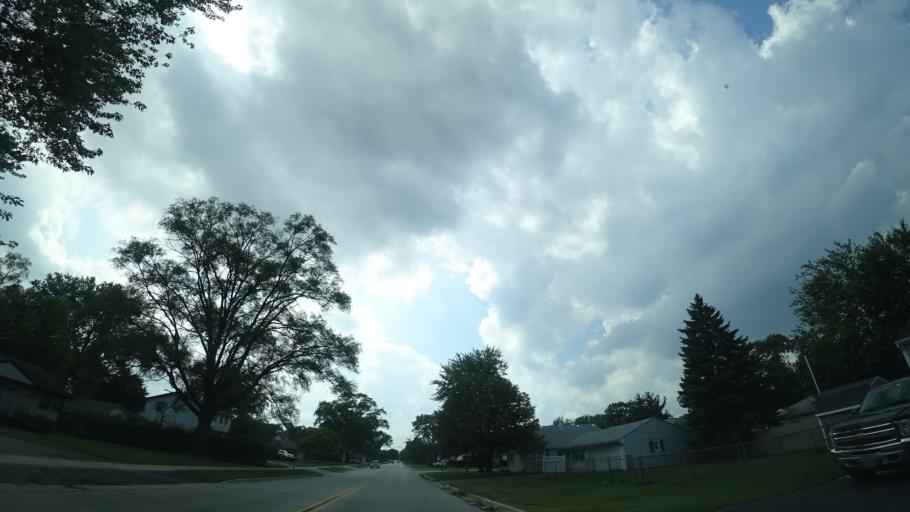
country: US
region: Illinois
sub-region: Cook County
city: Worth
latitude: 41.6829
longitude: -87.7838
